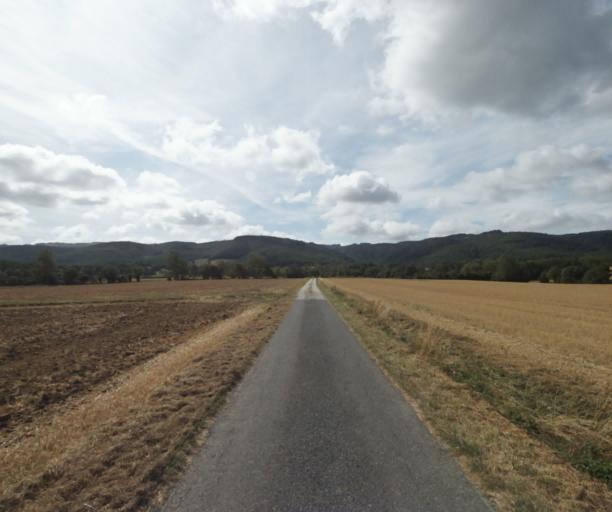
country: FR
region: Midi-Pyrenees
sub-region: Departement du Tarn
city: Soreze
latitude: 43.4733
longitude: 2.0994
